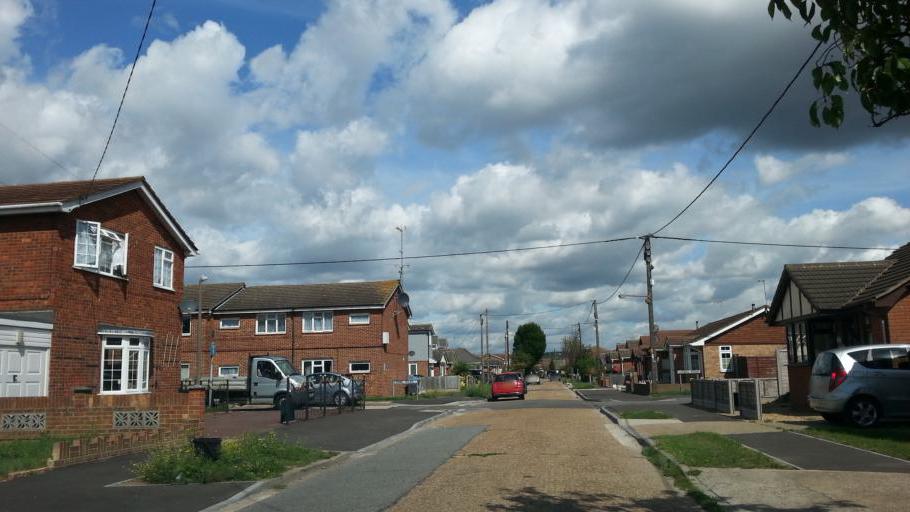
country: GB
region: England
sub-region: Essex
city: Canvey Island
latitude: 51.5208
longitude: 0.5850
